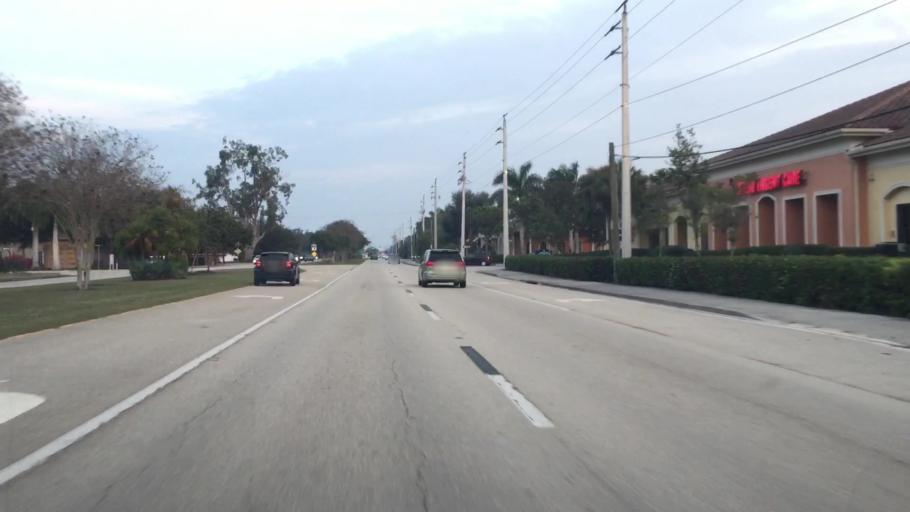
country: US
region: Florida
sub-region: Lee County
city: Estero
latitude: 26.4312
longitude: -81.8007
